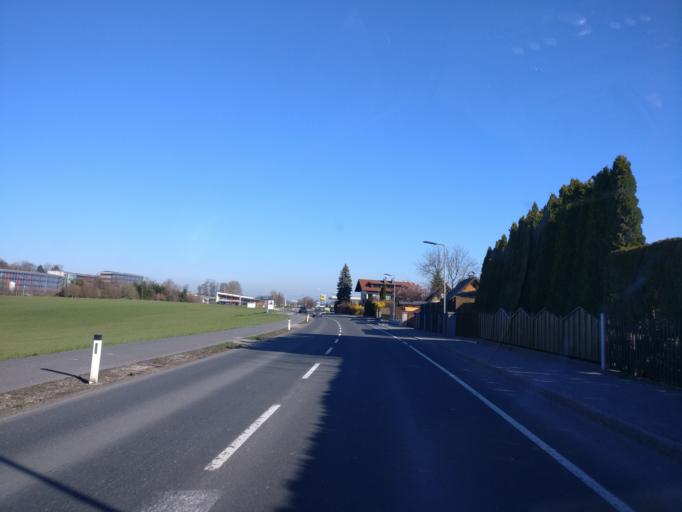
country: AT
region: Salzburg
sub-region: Politischer Bezirk Hallein
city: Puch bei Hallein
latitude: 47.7202
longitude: 13.0912
